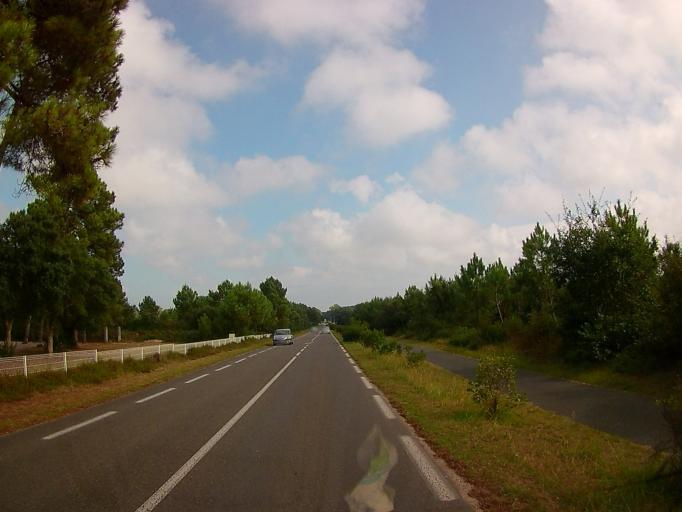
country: FR
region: Aquitaine
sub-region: Departement des Landes
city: Labenne
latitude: 43.5941
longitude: -1.4535
